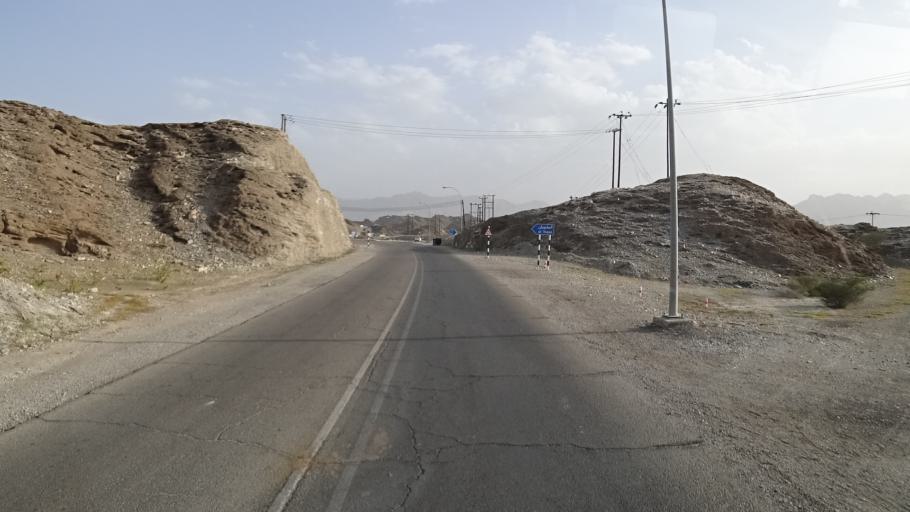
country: OM
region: Muhafazat Masqat
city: Bawshar
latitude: 23.3824
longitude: 58.5125
